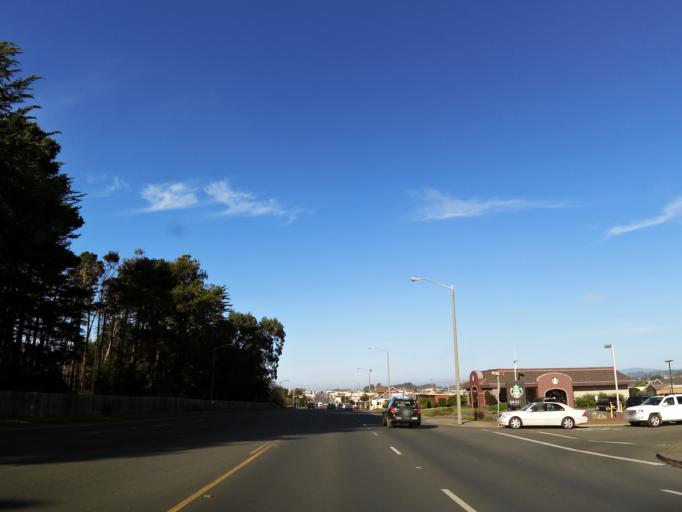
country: US
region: California
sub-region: Mendocino County
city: Fort Bragg
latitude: 39.4342
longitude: -123.8061
